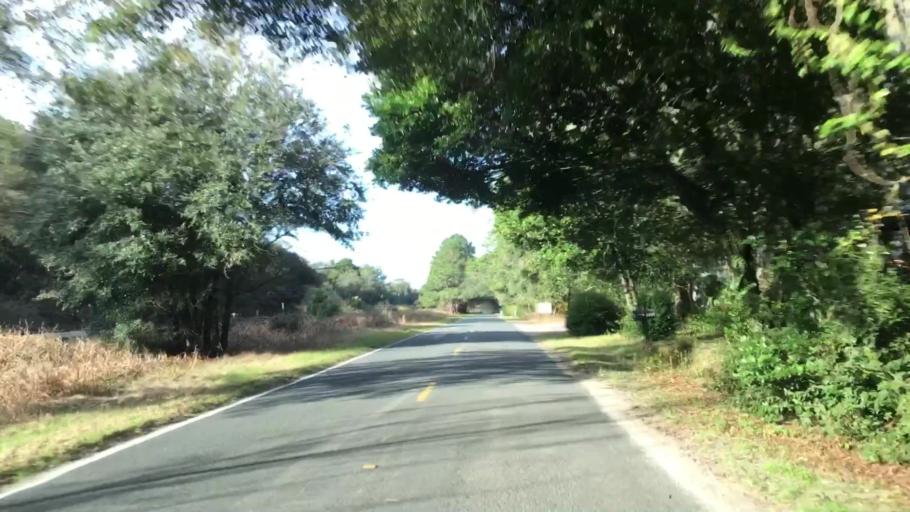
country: US
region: South Carolina
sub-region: Charleston County
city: Ravenel
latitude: 32.7661
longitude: -80.2278
